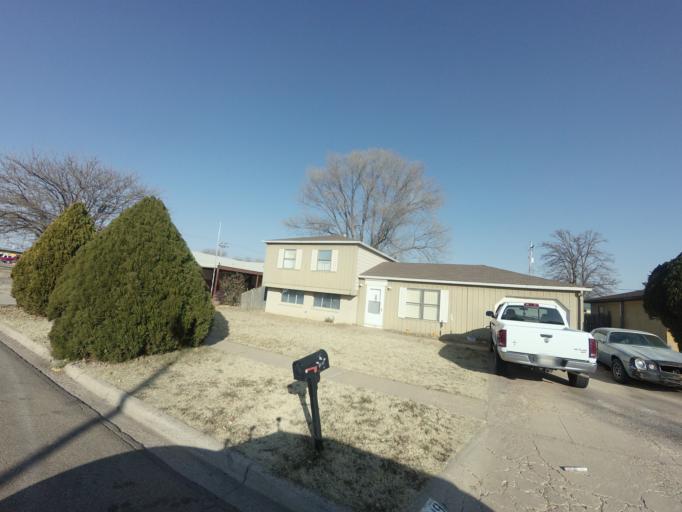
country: US
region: New Mexico
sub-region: Curry County
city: Clovis
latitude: 34.4153
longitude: -103.2135
